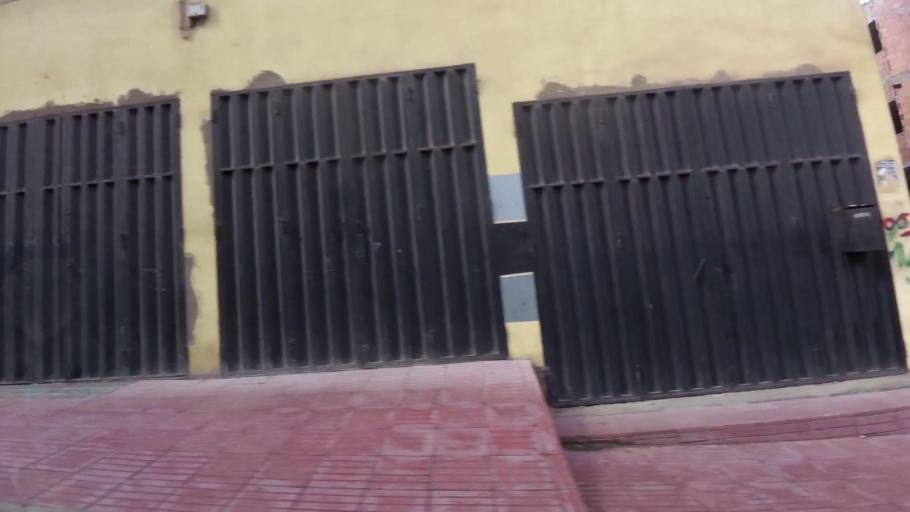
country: MA
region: Grand Casablanca
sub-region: Casablanca
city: Casablanca
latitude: 33.5379
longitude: -7.6826
